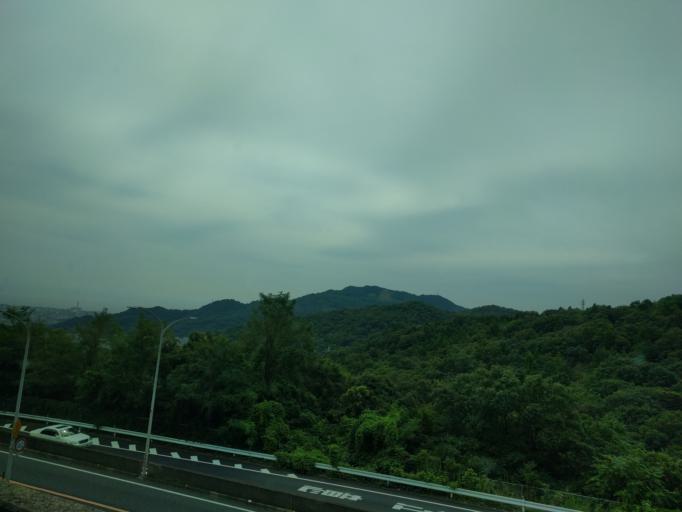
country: JP
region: Hyogo
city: Kobe
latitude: 34.6940
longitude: 135.1310
